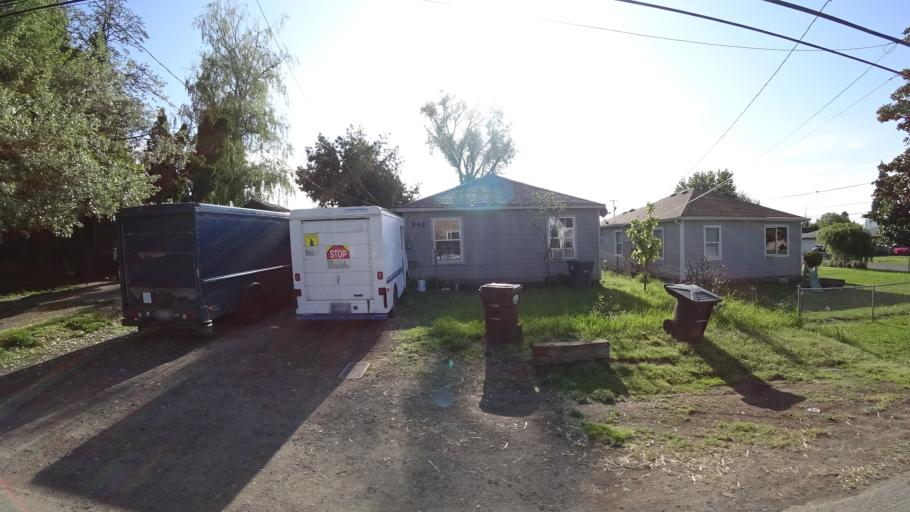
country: US
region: Oregon
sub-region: Washington County
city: Hillsboro
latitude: 45.5166
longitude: -122.9958
